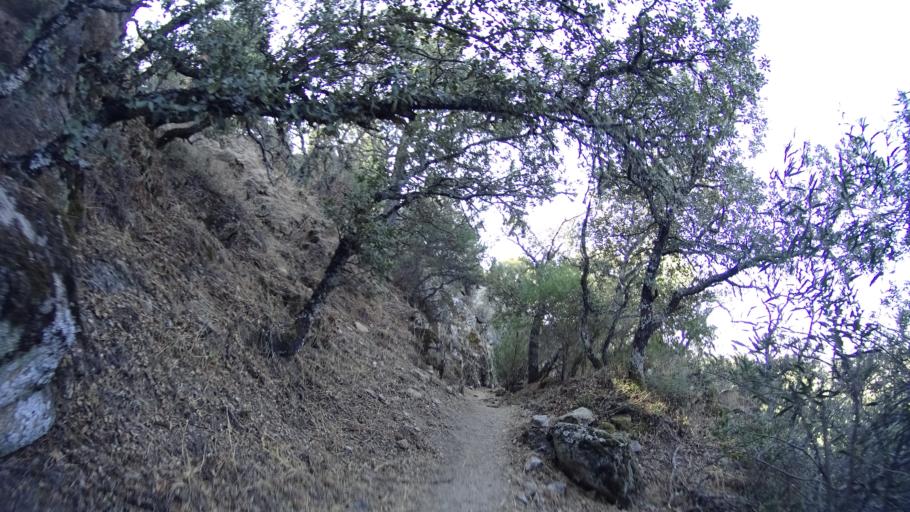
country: ES
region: Madrid
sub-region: Provincia de Madrid
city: Las Matas
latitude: 40.5794
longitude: -3.8950
